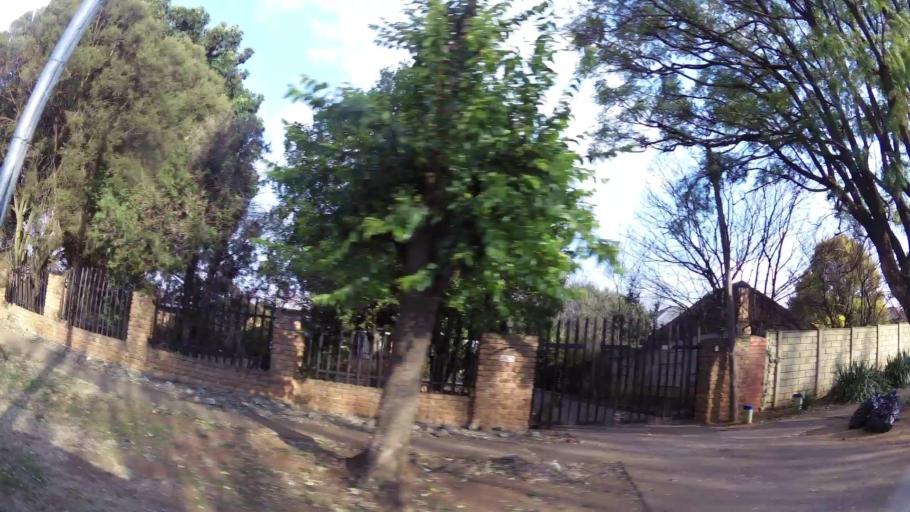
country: ZA
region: Gauteng
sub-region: Ekurhuleni Metropolitan Municipality
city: Springs
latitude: -26.2761
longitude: 28.4474
